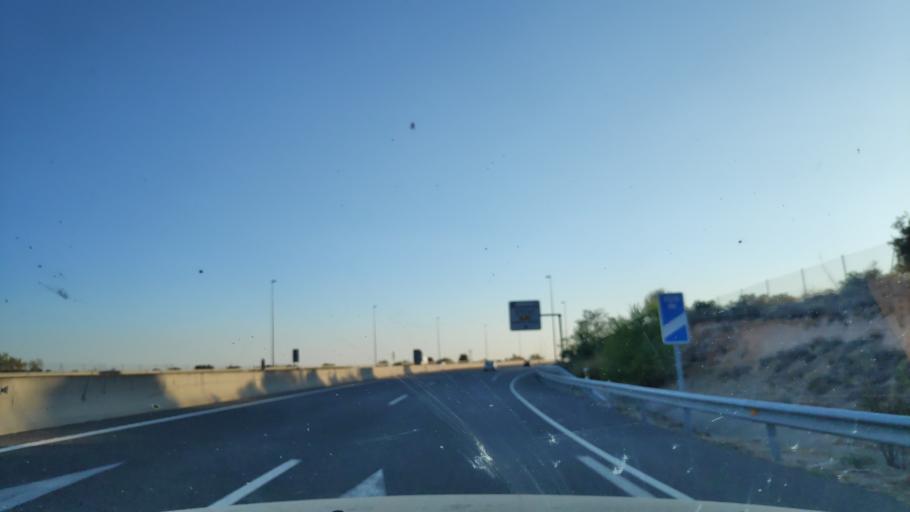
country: ES
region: Madrid
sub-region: Provincia de Madrid
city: Perales de Tajuna
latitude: 40.2586
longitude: -3.3672
